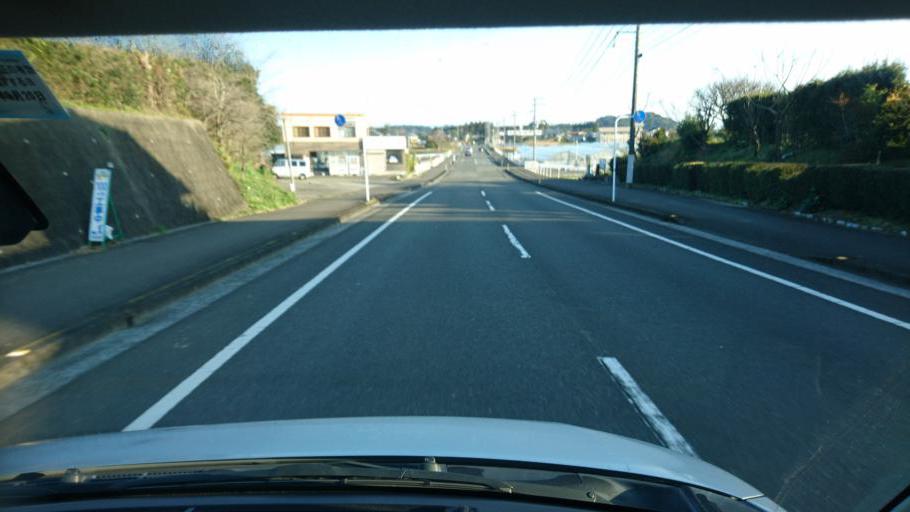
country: JP
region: Miyazaki
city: Miyazaki-shi
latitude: 31.8365
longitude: 131.4197
